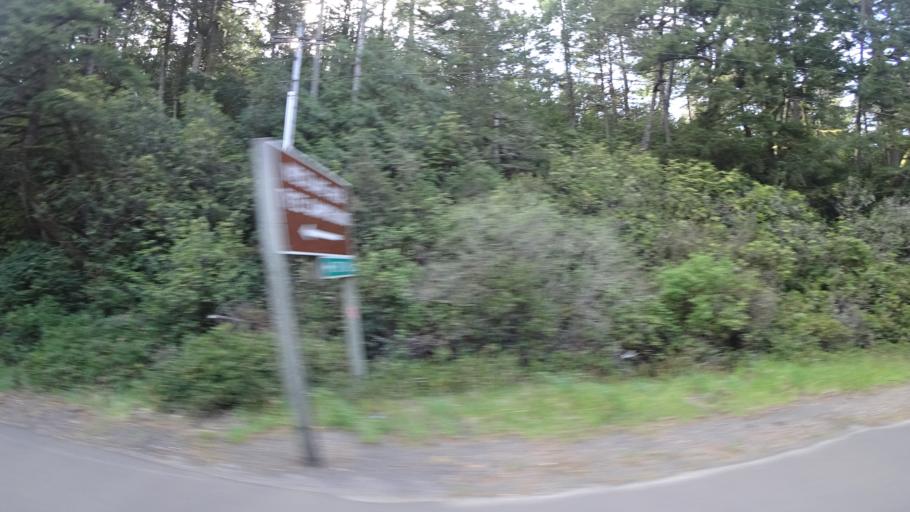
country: US
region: Oregon
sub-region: Lane County
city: Dunes City
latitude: 43.8848
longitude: -124.1213
